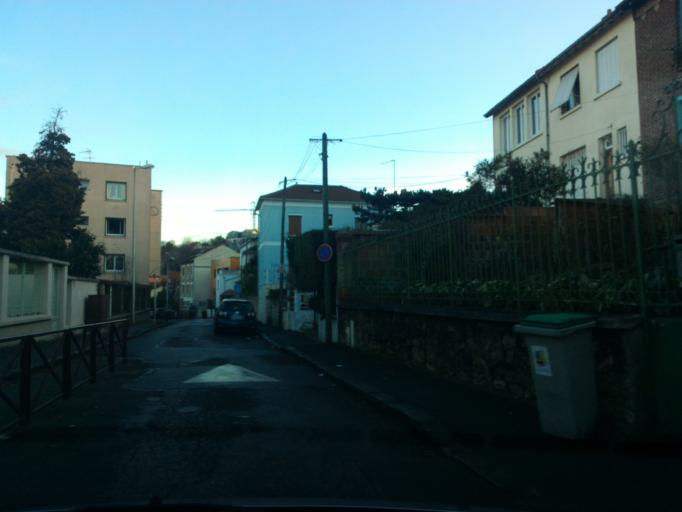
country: FR
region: Ile-de-France
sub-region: Departement du Val-de-Marne
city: Cachan
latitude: 48.7917
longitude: 2.3395
